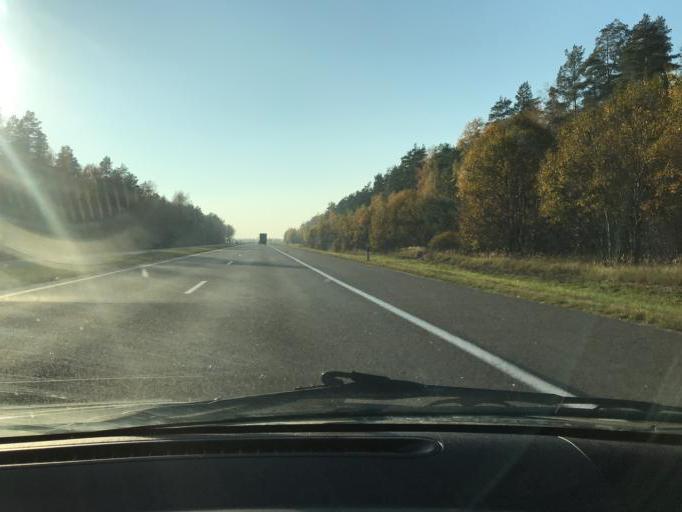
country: BY
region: Minsk
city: Loshnitsa
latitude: 54.2936
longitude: 28.8883
